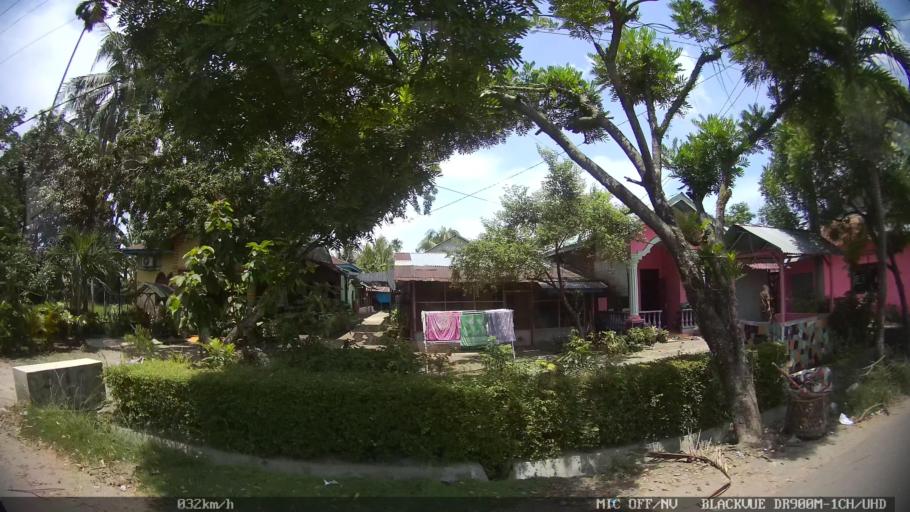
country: ID
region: North Sumatra
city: Binjai
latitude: 3.6047
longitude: 98.5180
